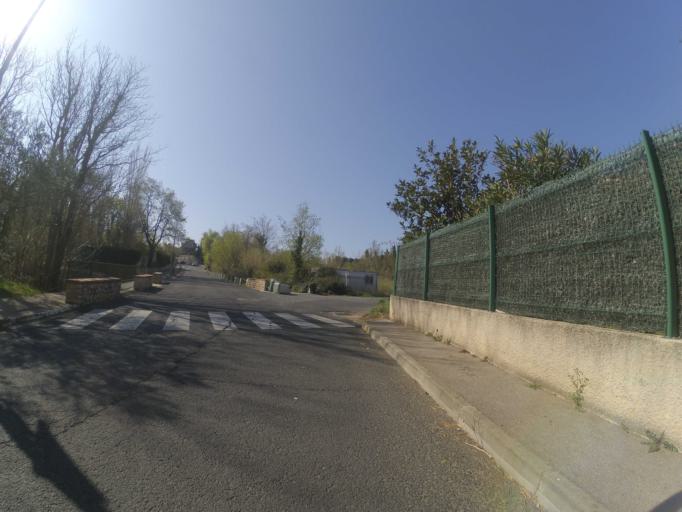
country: FR
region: Languedoc-Roussillon
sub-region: Departement des Pyrenees-Orientales
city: Thuir
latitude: 42.6265
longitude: 2.7508
